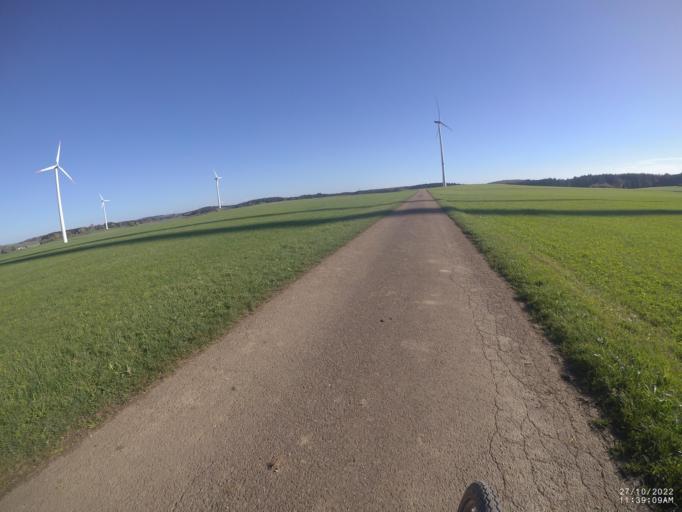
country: DE
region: Baden-Wuerttemberg
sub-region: Regierungsbezirk Stuttgart
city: Hohenstadt
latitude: 48.5475
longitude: 9.7017
